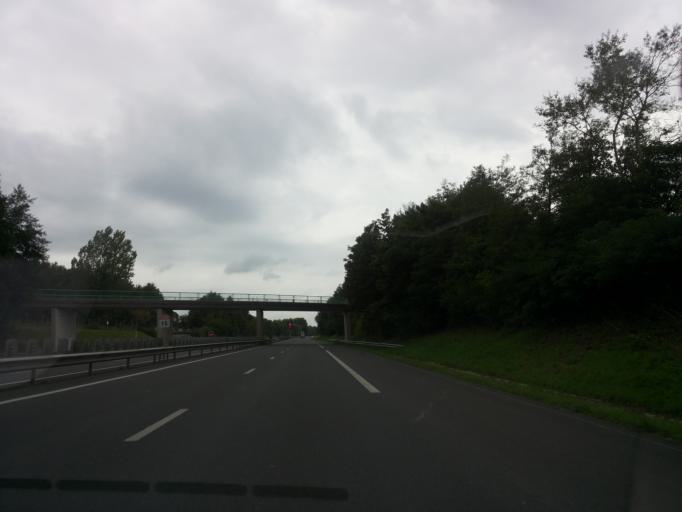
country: FR
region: Nord-Pas-de-Calais
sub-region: Departement du Pas-de-Calais
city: Nortkerque
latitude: 50.8458
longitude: 2.0362
